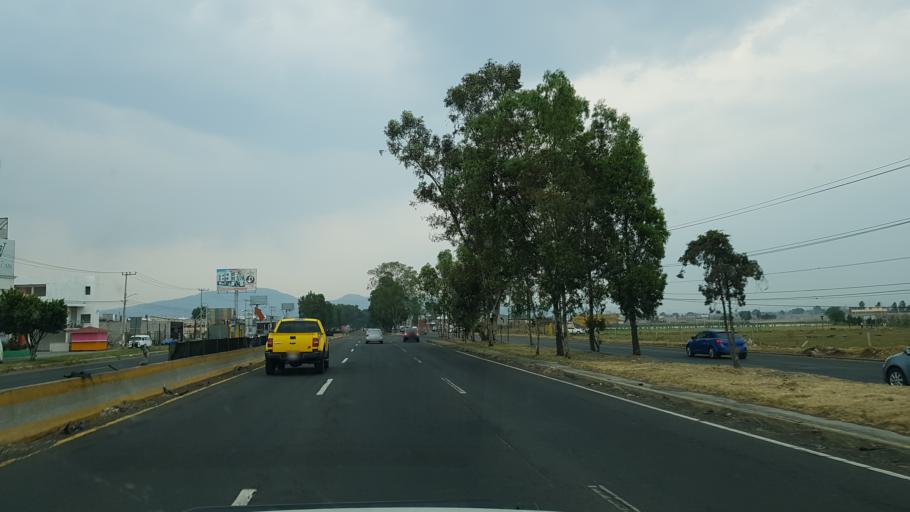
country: MX
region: Mexico
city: Chalco de Diaz Covarrubias
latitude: 19.2672
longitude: -98.8817
